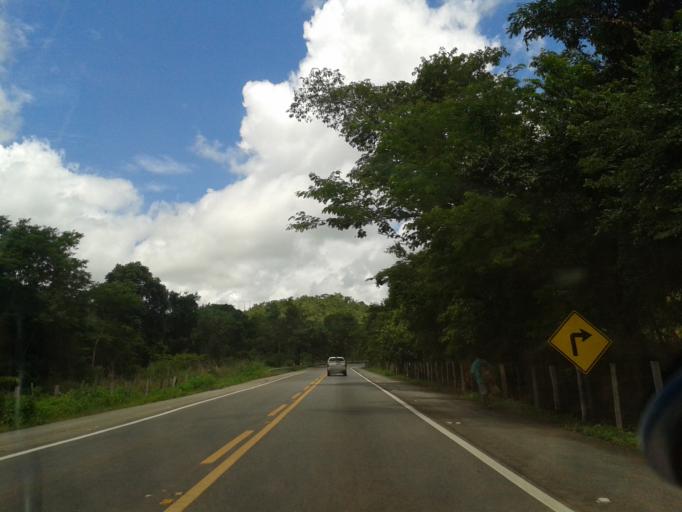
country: BR
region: Goias
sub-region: Goias
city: Goias
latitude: -15.8811
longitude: -50.1033
